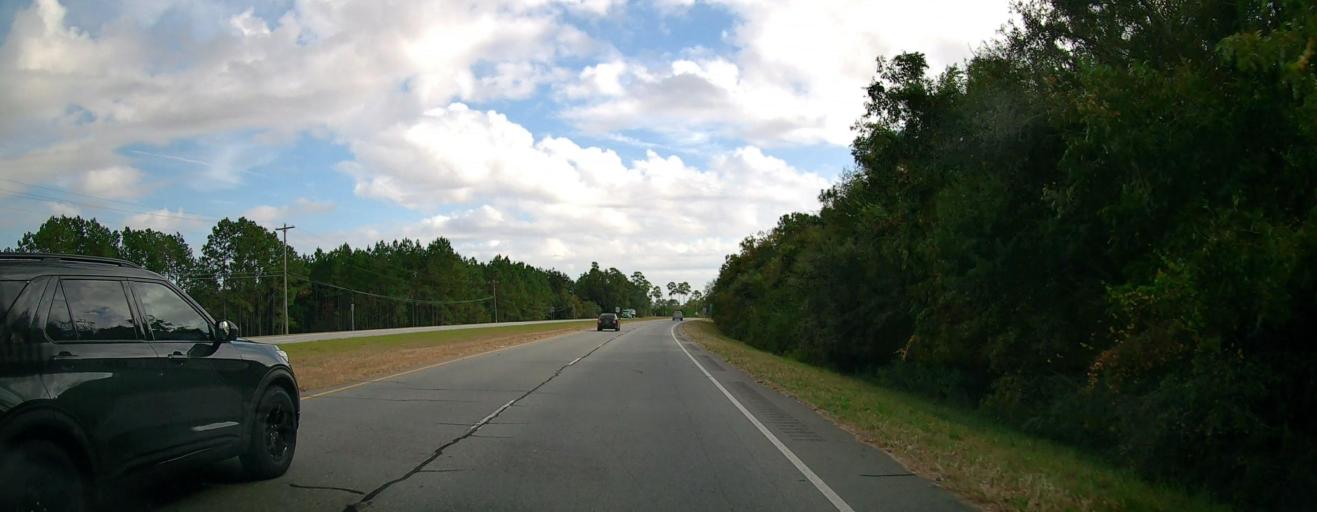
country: US
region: Georgia
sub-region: Mitchell County
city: Camilla
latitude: 31.2160
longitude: -84.1832
